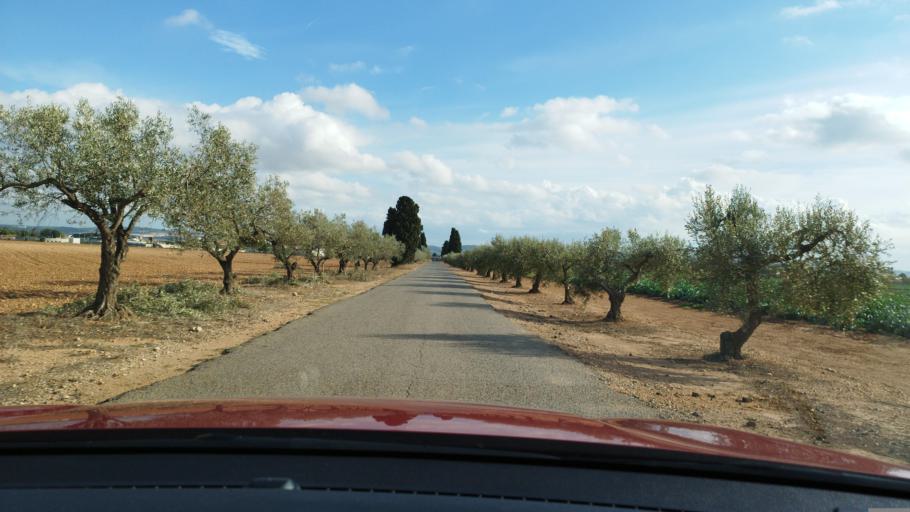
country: ES
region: Catalonia
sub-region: Provincia de Tarragona
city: Santa Oliva
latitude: 41.2561
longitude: 1.5305
